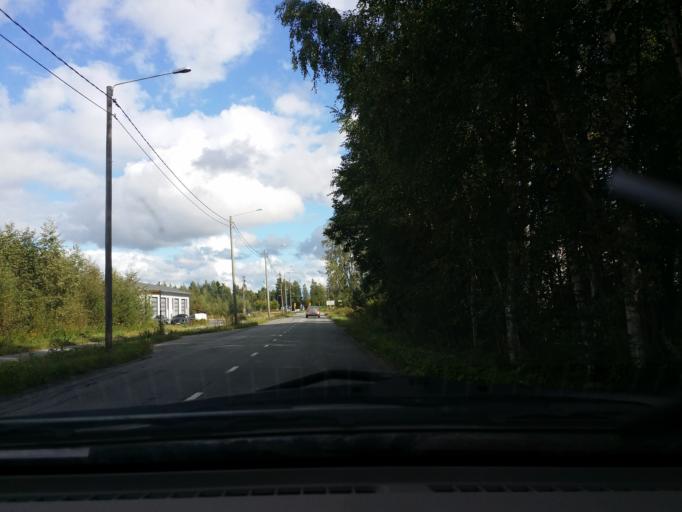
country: FI
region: Satakunta
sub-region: Pori
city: Pori
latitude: 61.4936
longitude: 21.8357
